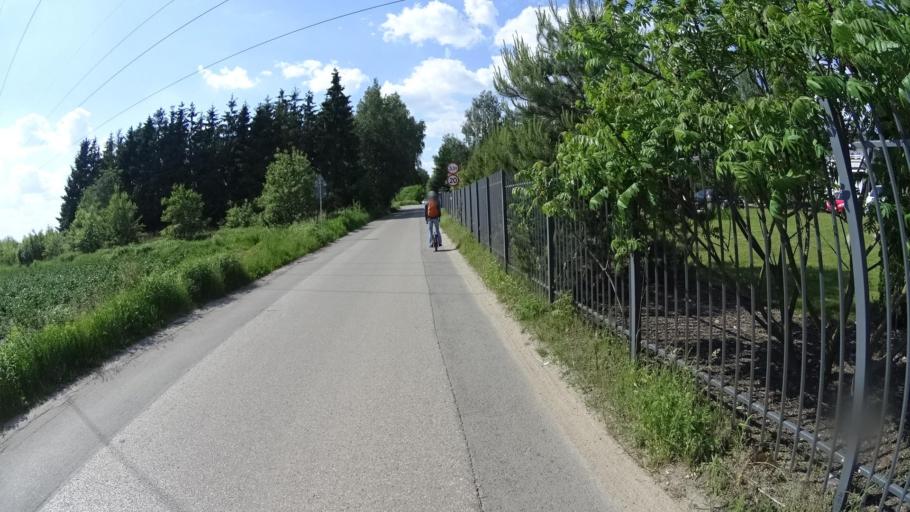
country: PL
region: Masovian Voivodeship
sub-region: Powiat piaseczynski
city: Jozefoslaw
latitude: 52.0964
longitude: 21.0734
